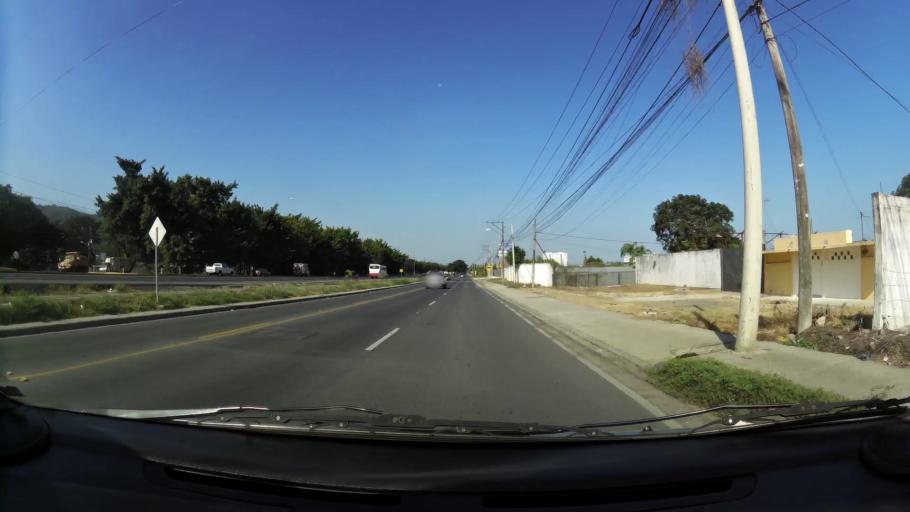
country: EC
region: Guayas
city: Santa Lucia
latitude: -2.1850
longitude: -79.9757
